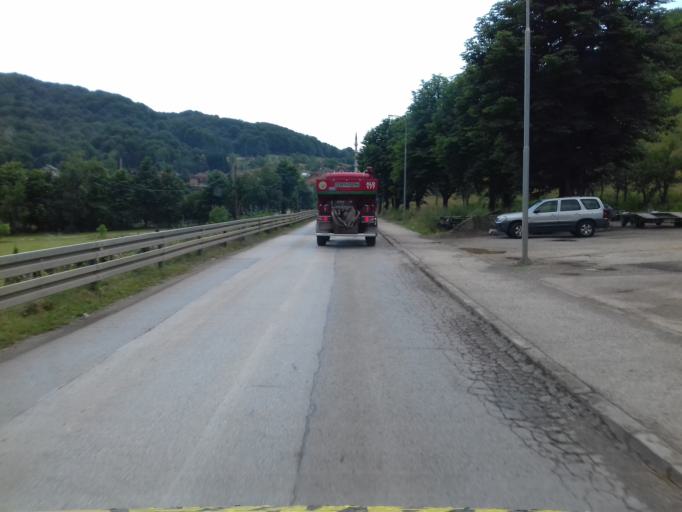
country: BA
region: Federation of Bosnia and Herzegovina
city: Visoko
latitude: 43.9656
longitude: 18.1832
